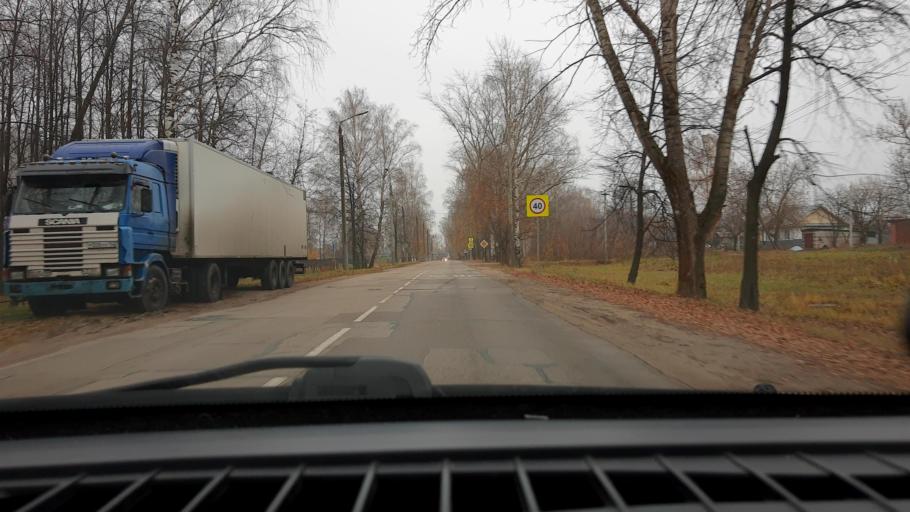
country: RU
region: Nizjnij Novgorod
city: Kstovo
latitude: 56.1812
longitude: 44.1579
